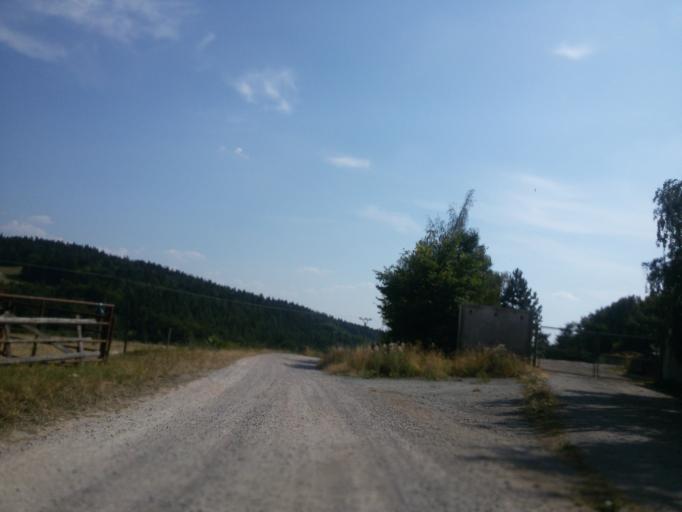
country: CZ
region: South Moravian
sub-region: Okres Brno-Venkov
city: Lomnice
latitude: 49.4408
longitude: 16.4558
